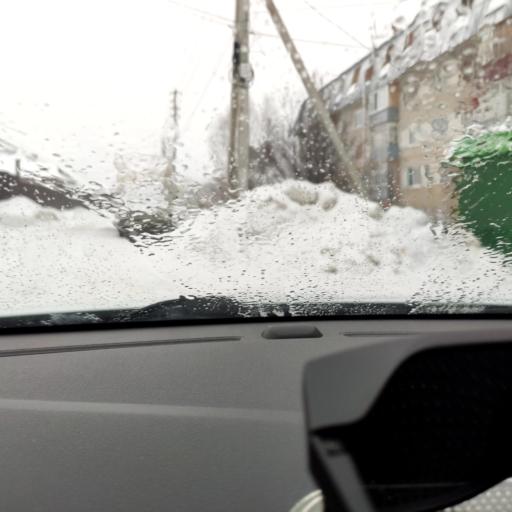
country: RU
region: Tatarstan
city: Vysokaya Gora
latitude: 55.9359
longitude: 49.2997
